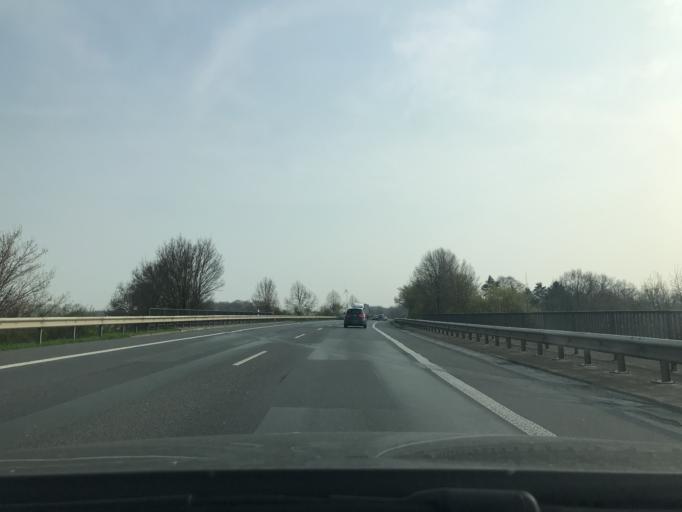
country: DE
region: North Rhine-Westphalia
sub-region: Regierungsbezirk Dusseldorf
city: Kevelaer
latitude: 51.5714
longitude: 6.2637
